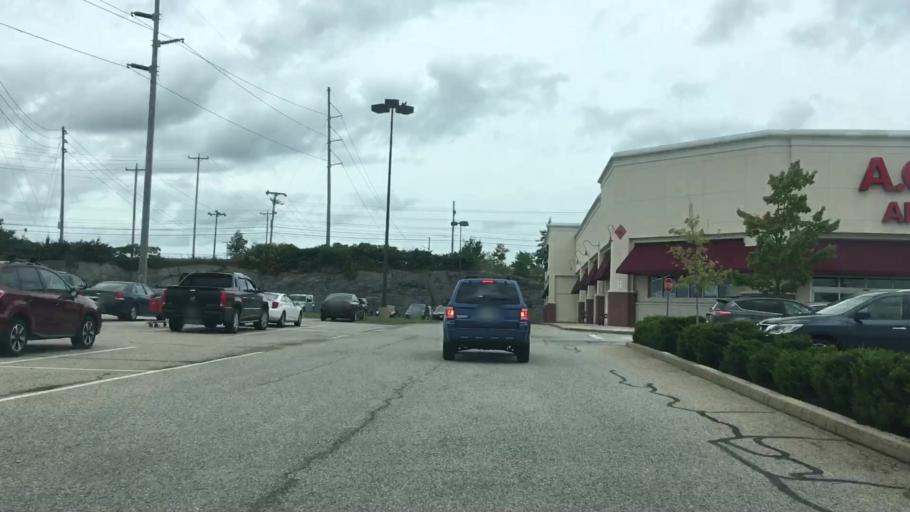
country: US
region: Maine
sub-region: Cumberland County
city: South Portland Gardens
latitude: 43.6342
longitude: -70.3459
